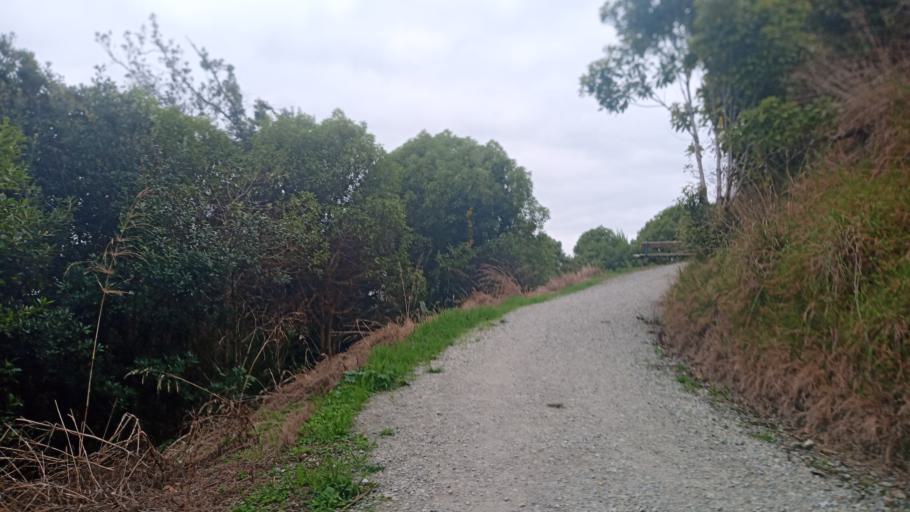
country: NZ
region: Gisborne
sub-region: Gisborne District
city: Gisborne
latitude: -38.6745
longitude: 178.0276
